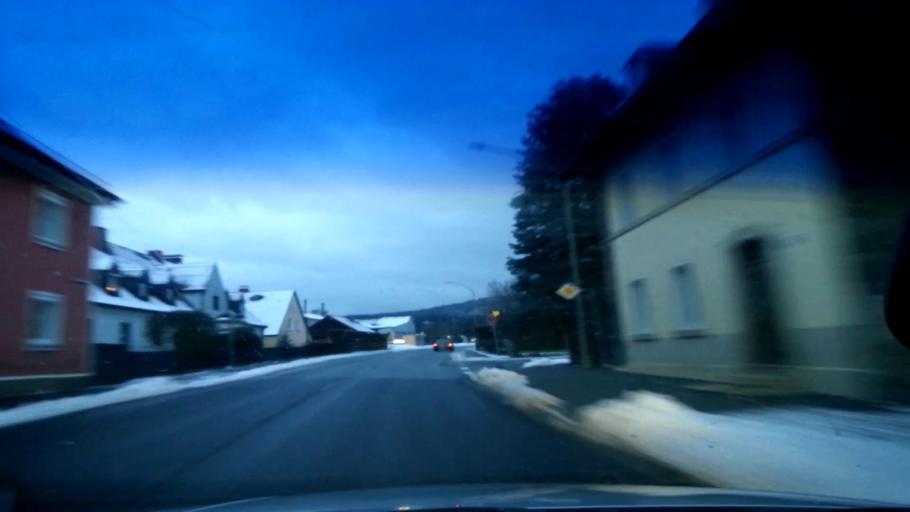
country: DE
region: Bavaria
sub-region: Upper Franconia
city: Kirchenlamitz
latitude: 50.1498
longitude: 11.9436
